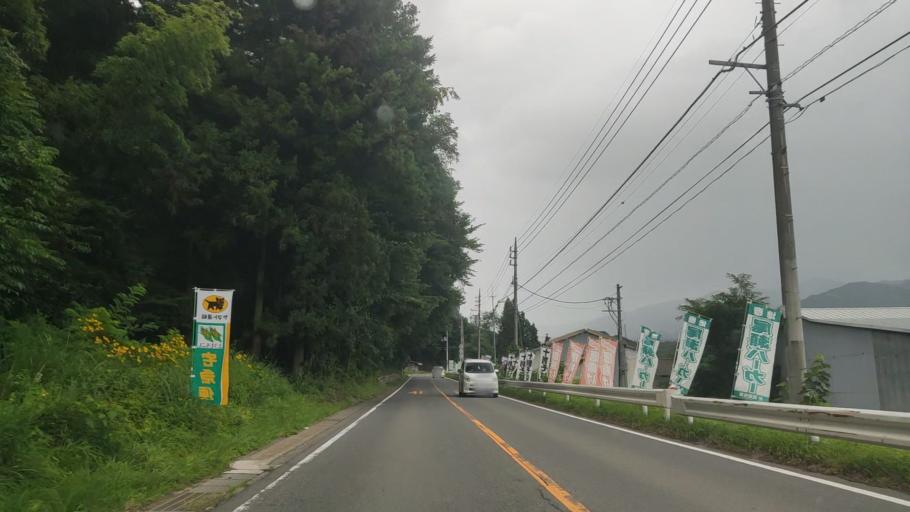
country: JP
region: Gunma
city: Numata
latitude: 36.7159
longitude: 139.2114
